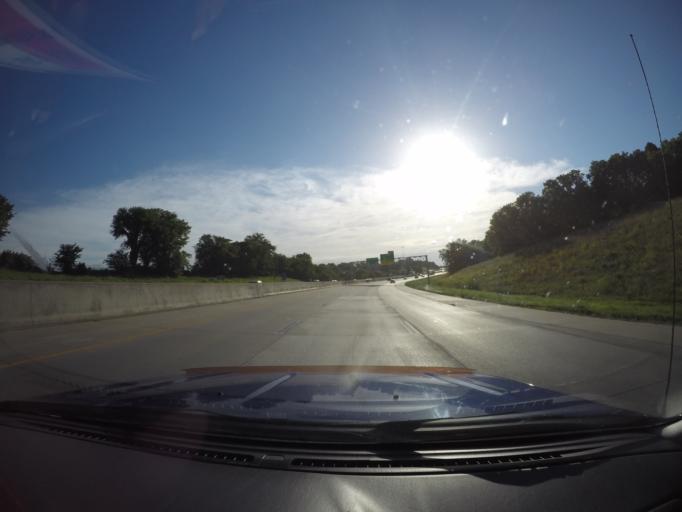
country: US
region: Kansas
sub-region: Wyandotte County
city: Kansas City
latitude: 39.1462
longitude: -94.6668
